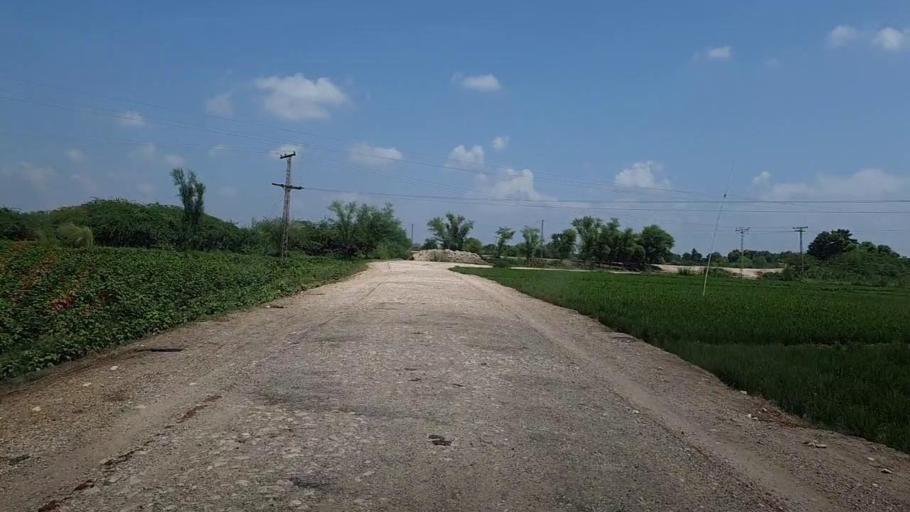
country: PK
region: Sindh
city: Kandiaro
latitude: 26.9864
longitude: 68.2413
